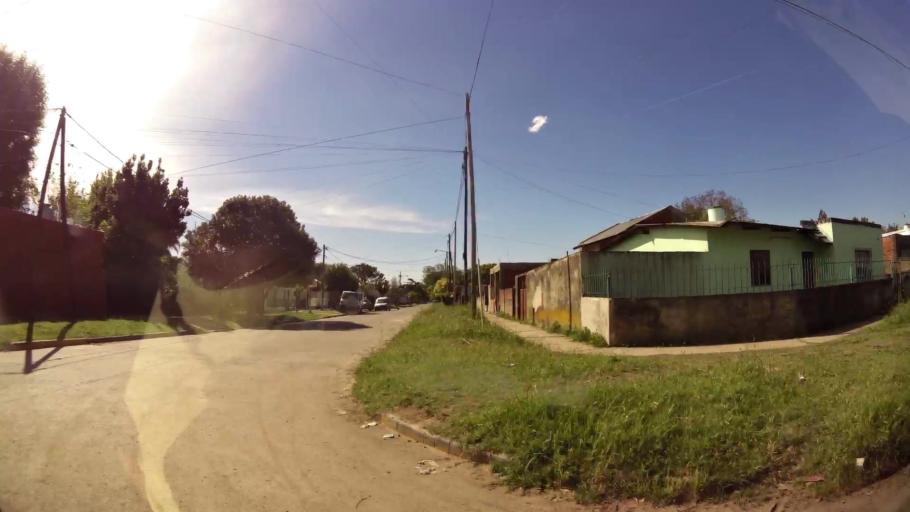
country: AR
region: Buenos Aires
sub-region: Partido de Almirante Brown
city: Adrogue
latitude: -34.8033
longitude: -58.3615
